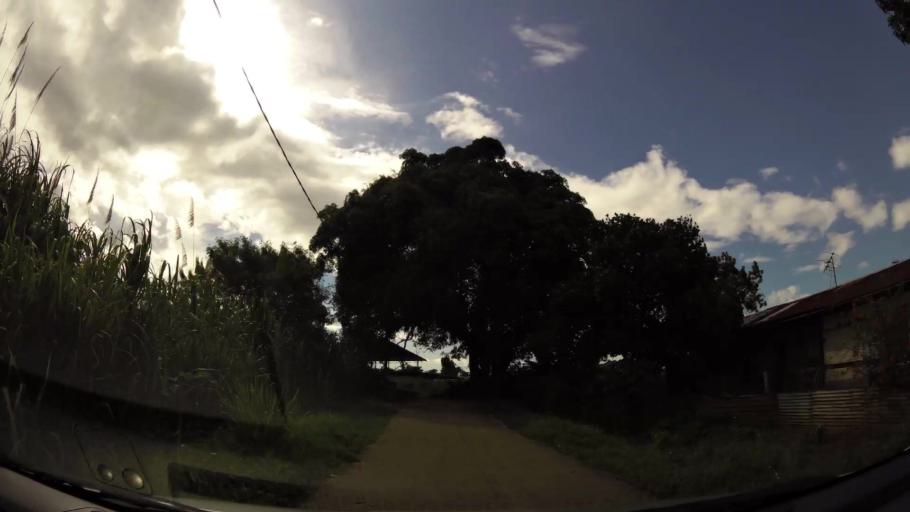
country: SR
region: Paramaribo
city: Paramaribo
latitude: 5.8525
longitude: -55.1610
